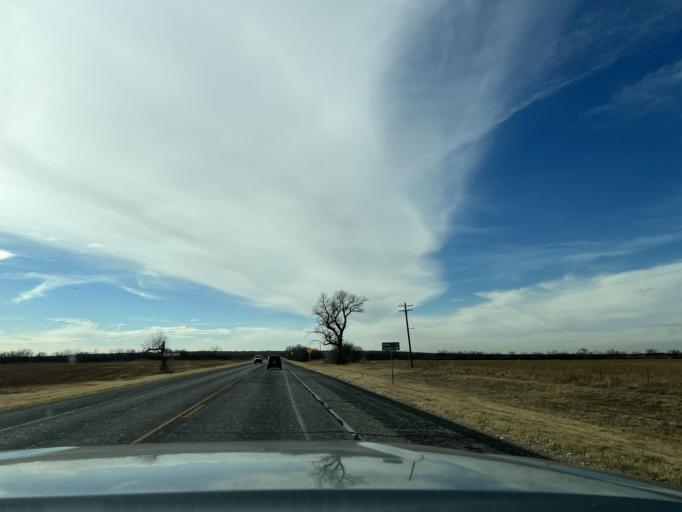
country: US
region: Texas
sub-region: Fisher County
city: Roby
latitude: 32.7612
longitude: -100.3031
